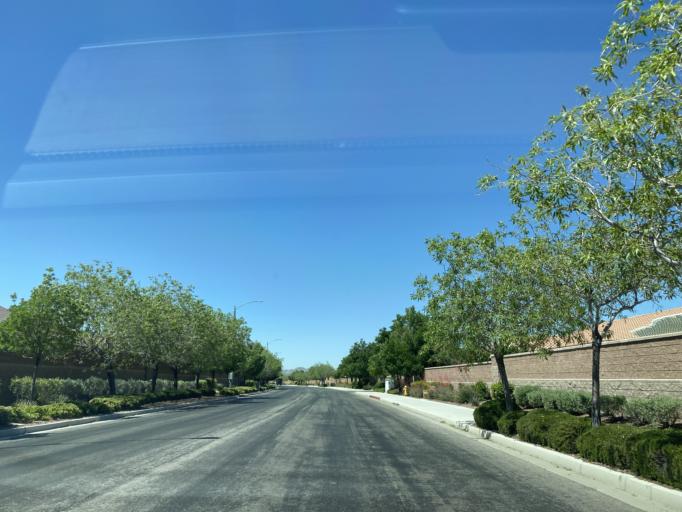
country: US
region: Nevada
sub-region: Clark County
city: Whitney
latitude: 35.9433
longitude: -115.0865
